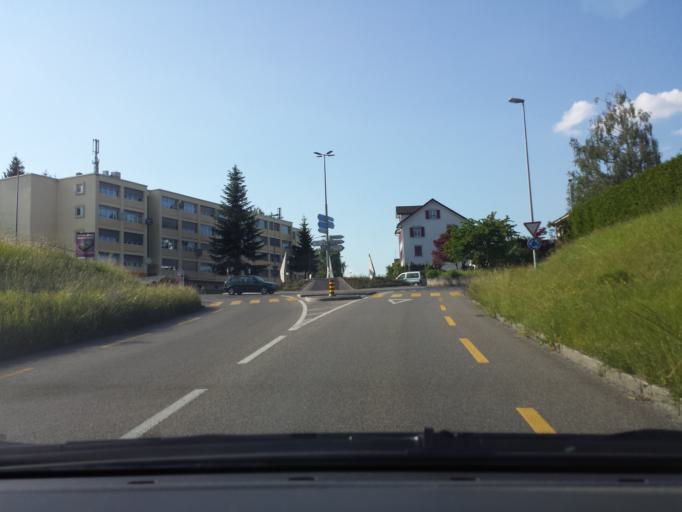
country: CH
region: Thurgau
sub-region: Arbon District
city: Salmsach
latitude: 47.5583
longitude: 9.3694
